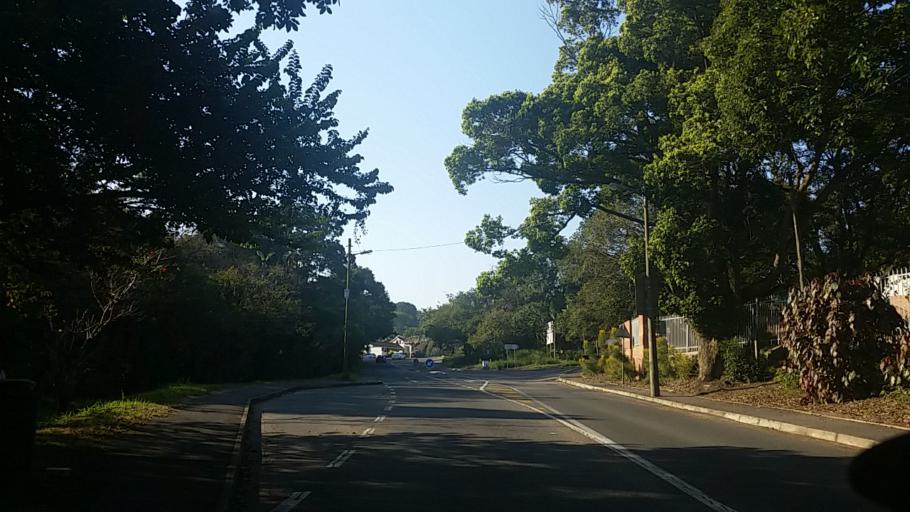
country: ZA
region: KwaZulu-Natal
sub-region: eThekwini Metropolitan Municipality
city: Berea
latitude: -29.8389
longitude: 30.9240
